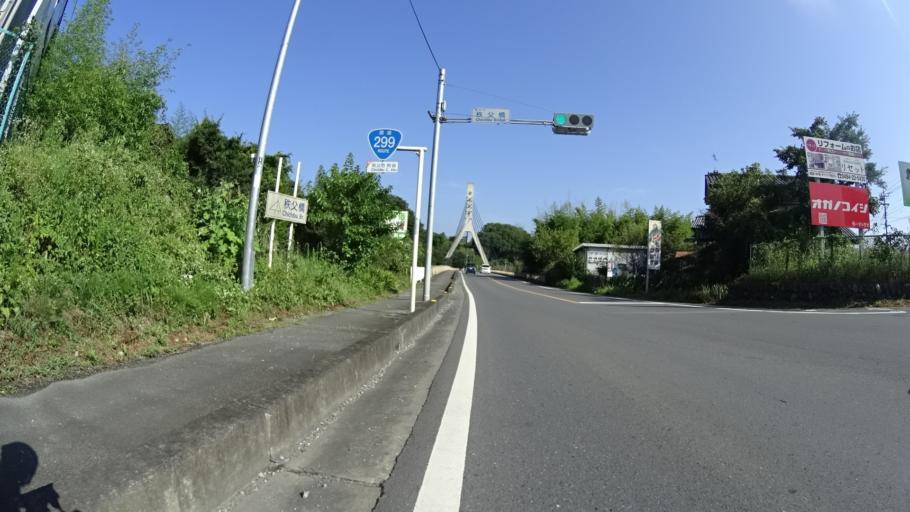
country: JP
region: Saitama
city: Chichibu
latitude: 36.0171
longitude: 139.0864
